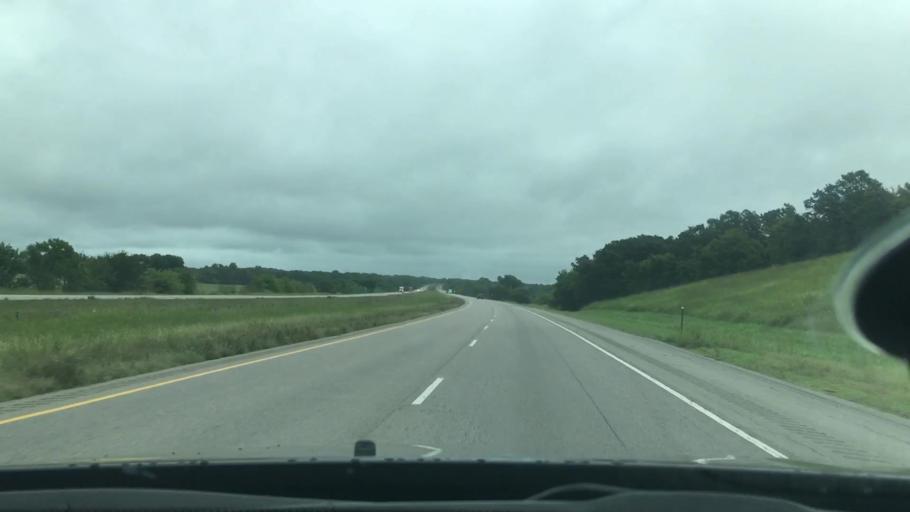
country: US
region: Oklahoma
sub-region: Okfuskee County
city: Okemah
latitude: 35.3879
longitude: -96.4150
